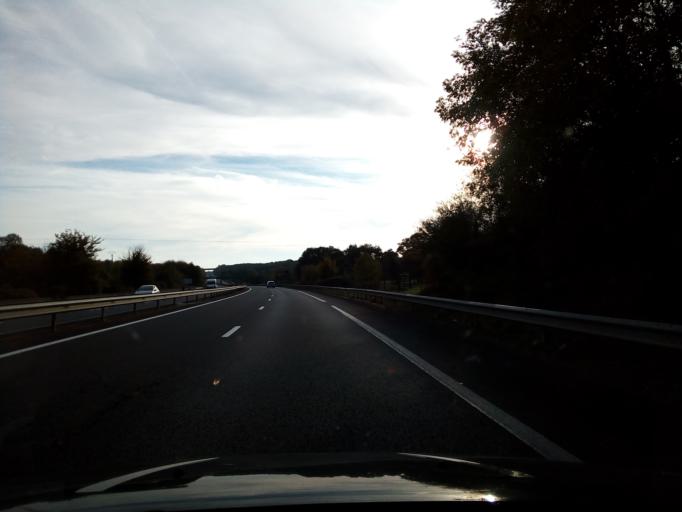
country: FR
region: Poitou-Charentes
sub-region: Departement de la Charente
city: Taponnat-Fleurignac
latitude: 45.7826
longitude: 0.4082
